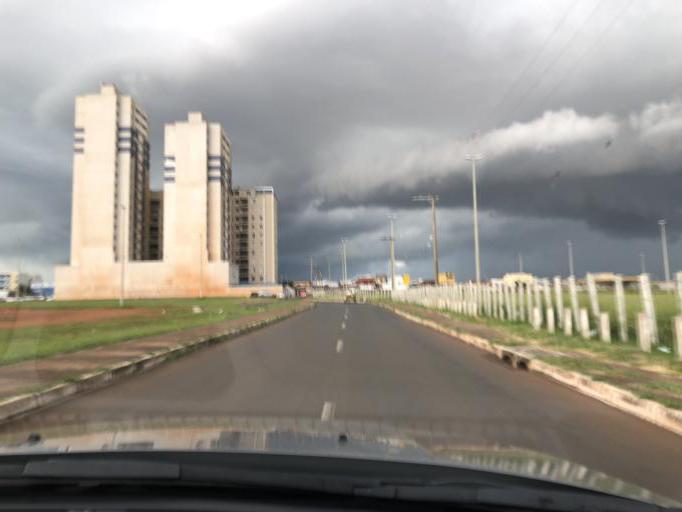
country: BR
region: Federal District
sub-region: Brasilia
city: Brasilia
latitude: -15.8257
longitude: -48.1124
